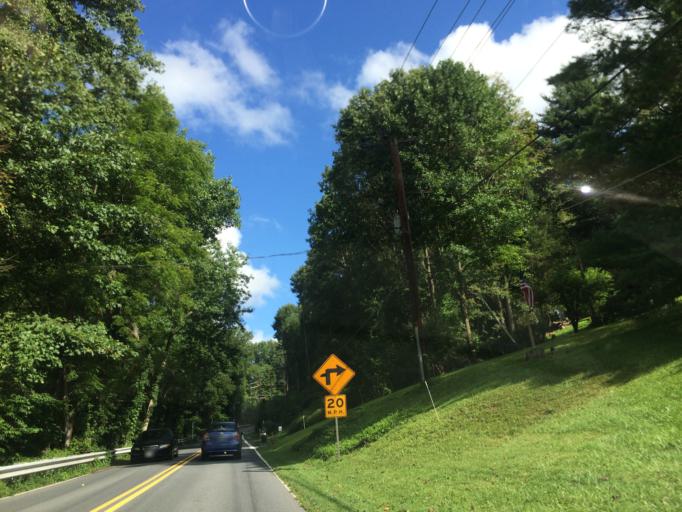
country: US
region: Maryland
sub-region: Carroll County
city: Eldersburg
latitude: 39.3756
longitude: -76.9104
